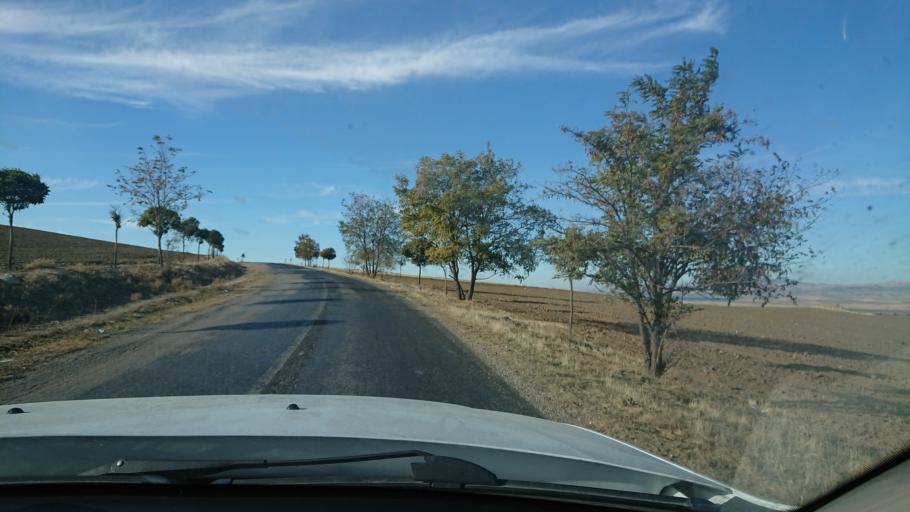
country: TR
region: Aksaray
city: Sariyahsi
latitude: 38.9712
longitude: 33.8658
